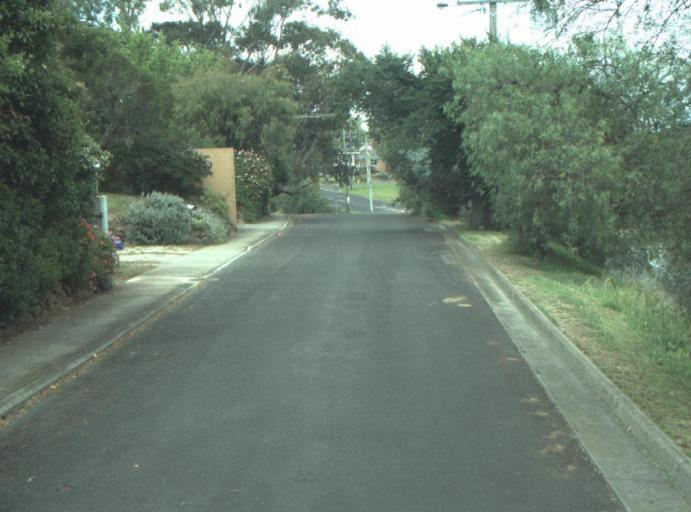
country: AU
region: Victoria
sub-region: Greater Geelong
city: Wandana Heights
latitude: -38.1676
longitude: 144.3325
